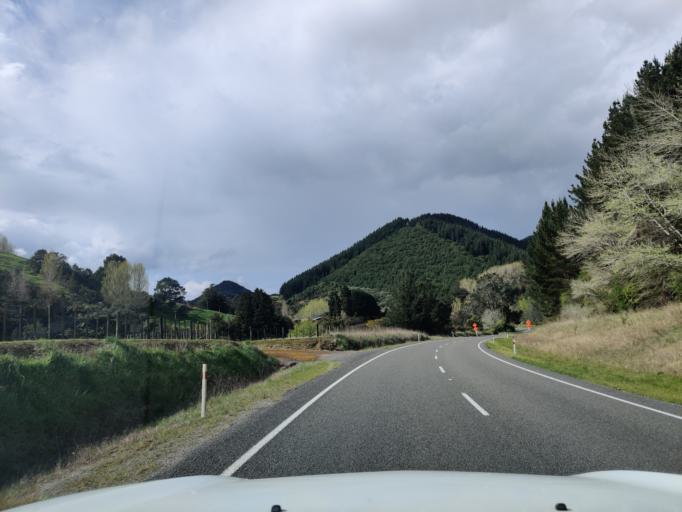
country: NZ
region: Manawatu-Wanganui
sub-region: Wanganui District
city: Wanganui
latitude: -39.8145
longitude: 175.1841
